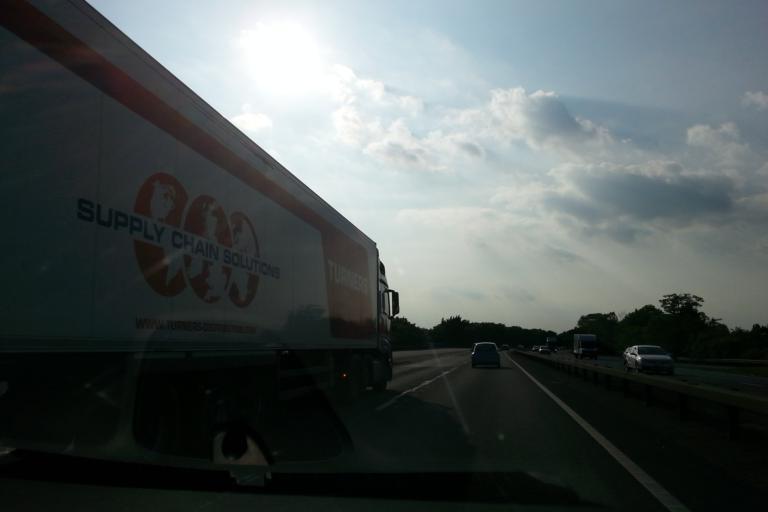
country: GB
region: England
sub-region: Cambridgeshire
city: Godmanchester
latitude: 52.3200
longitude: -0.1612
